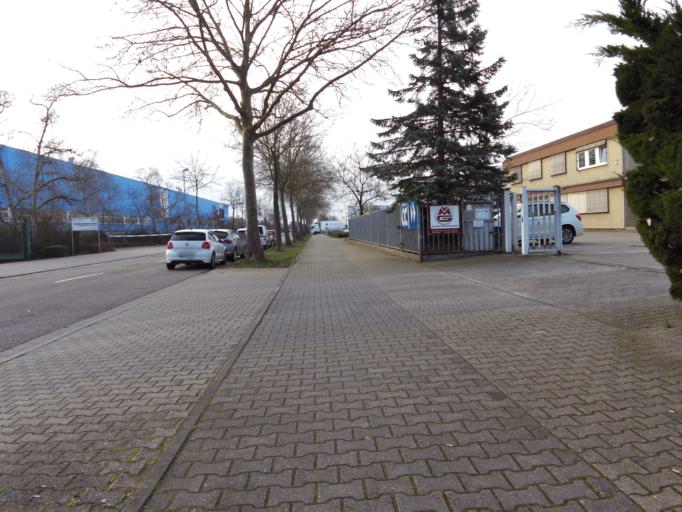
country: DE
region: Rheinland-Pfalz
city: Worms
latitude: 49.6113
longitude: 8.3461
